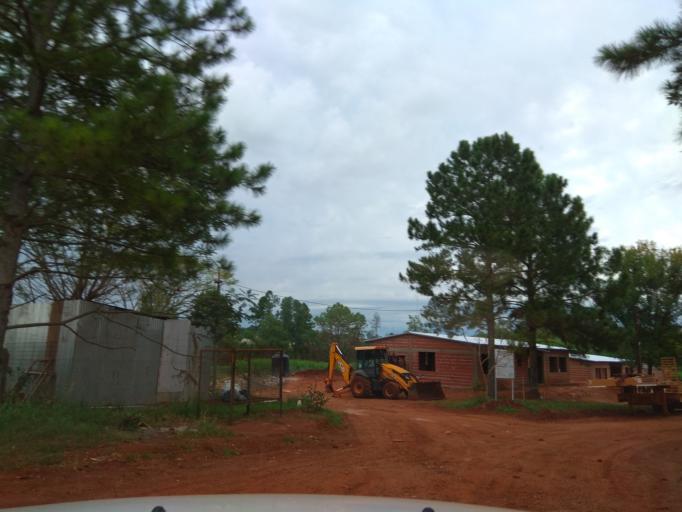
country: AR
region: Misiones
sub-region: Departamento de Capital
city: Posadas
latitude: -27.4381
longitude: -55.8926
